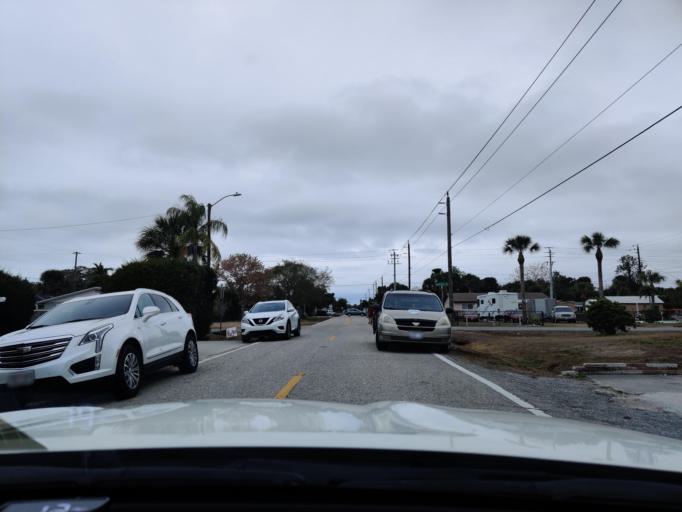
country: US
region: Florida
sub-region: Sarasota County
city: South Venice
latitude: 27.0440
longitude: -82.4142
